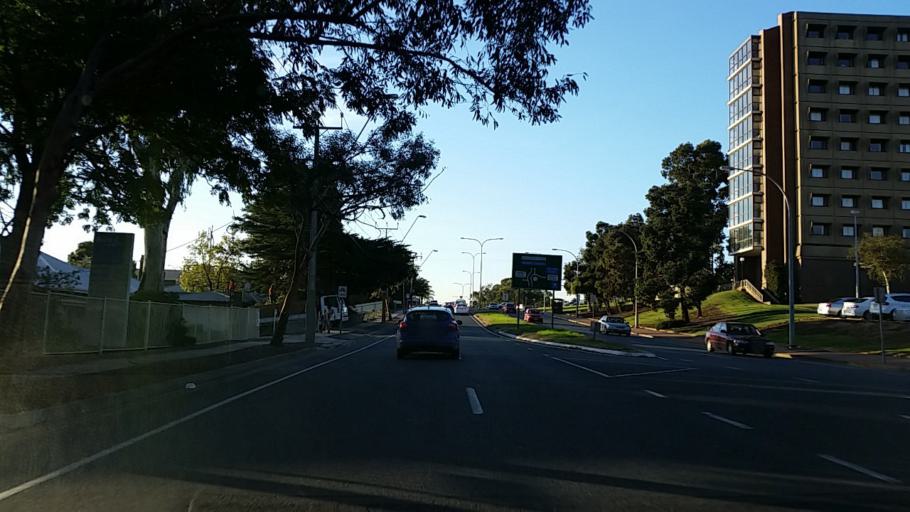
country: AU
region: South Australia
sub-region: Tea Tree Gully
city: Modbury
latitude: -34.8353
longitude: 138.6882
